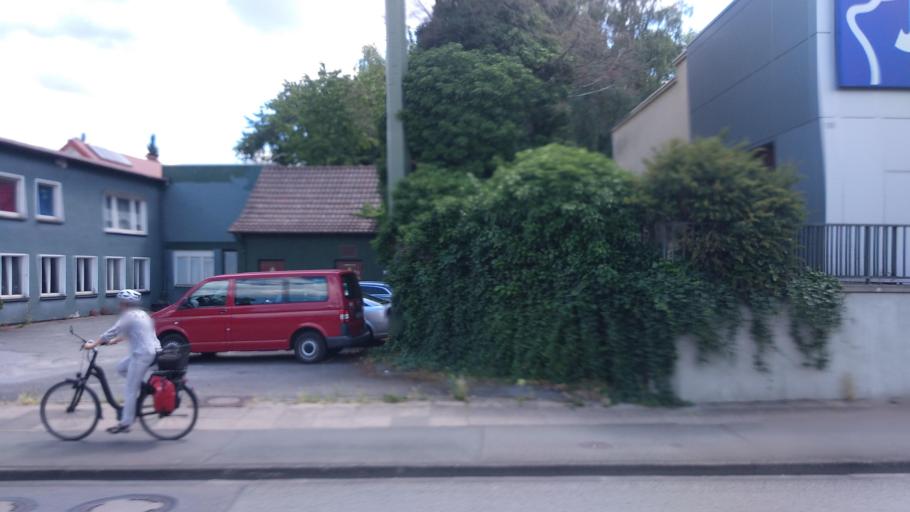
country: DE
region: North Rhine-Westphalia
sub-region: Regierungsbezirk Detmold
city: Bielefeld
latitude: 52.0036
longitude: 8.5074
